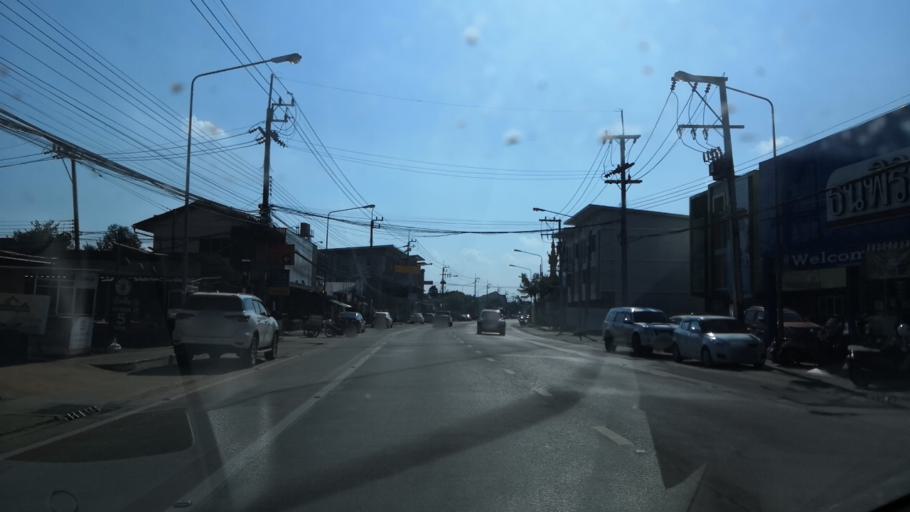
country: TH
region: Chiang Rai
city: Chiang Rai
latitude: 19.9290
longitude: 99.8387
